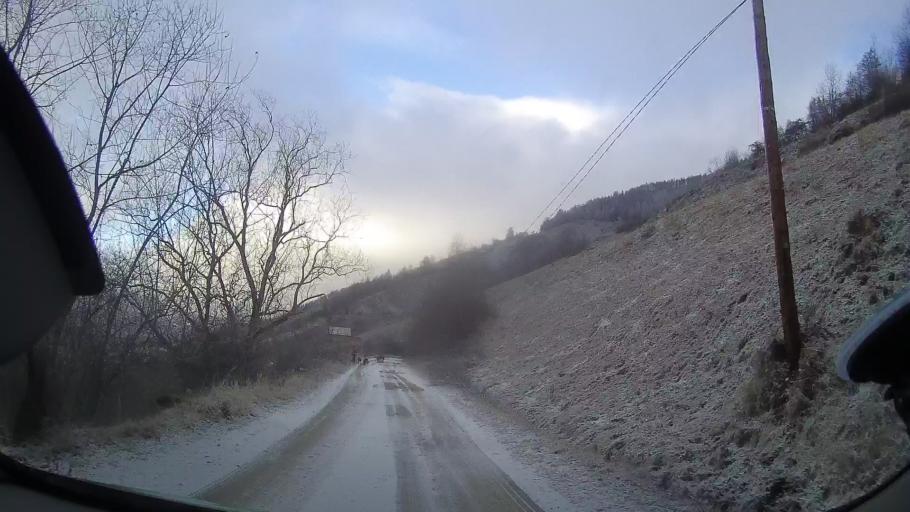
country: RO
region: Cluj
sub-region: Comuna Valea Ierii
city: Valea Ierii
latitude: 46.6675
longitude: 23.3316
